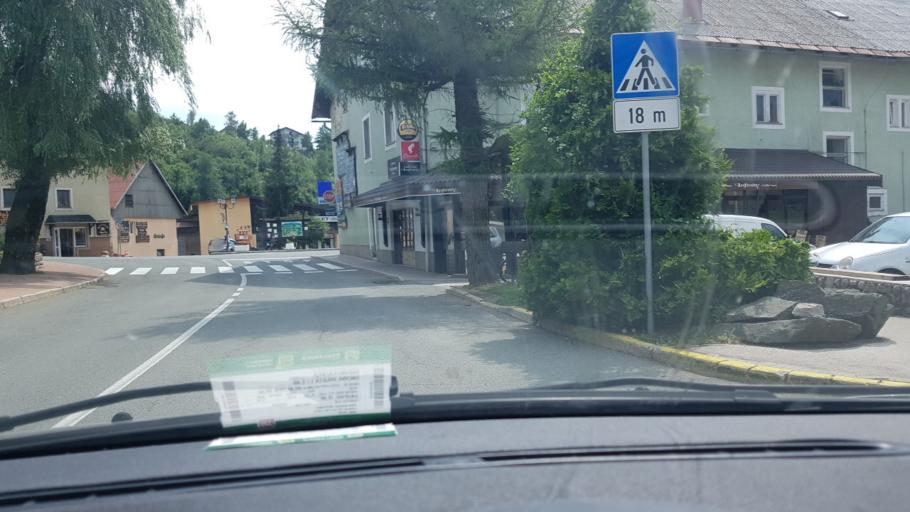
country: HR
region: Primorsko-Goranska
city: Hreljin
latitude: 45.3050
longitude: 14.7135
